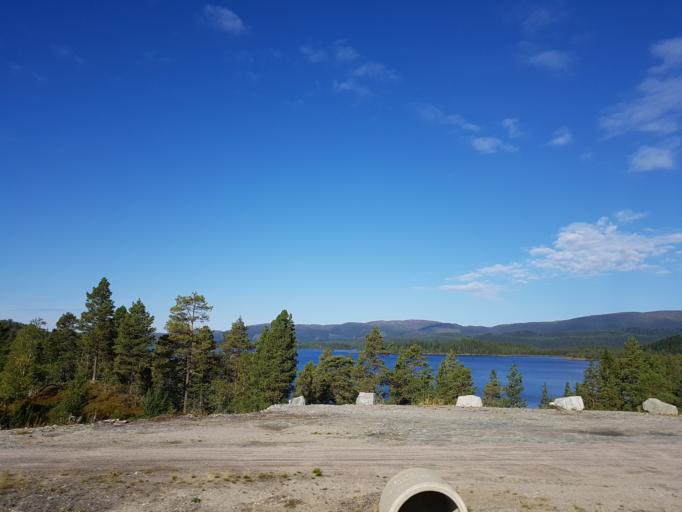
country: NO
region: Sor-Trondelag
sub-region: Trondheim
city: Trondheim
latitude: 63.6265
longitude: 10.2477
